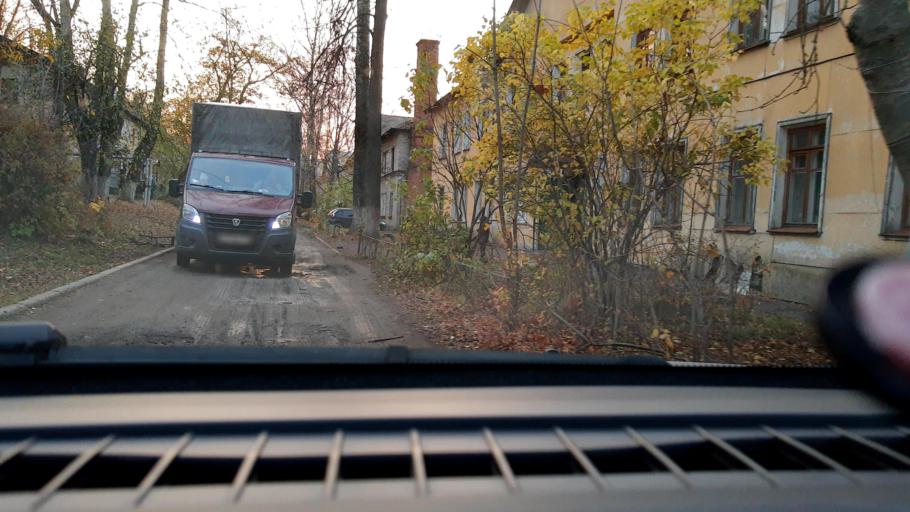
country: RU
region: Nizjnij Novgorod
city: Nizhniy Novgorod
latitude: 56.2937
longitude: 43.9980
